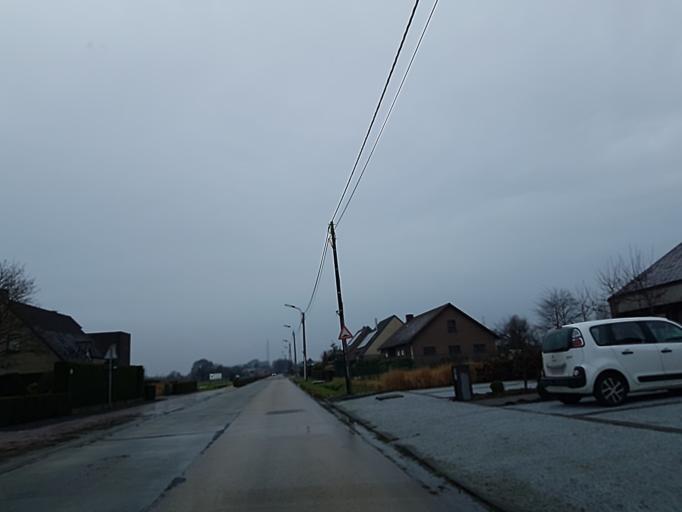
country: BE
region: Flanders
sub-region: Provincie Antwerpen
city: Sint-Amands
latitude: 51.0633
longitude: 4.2364
